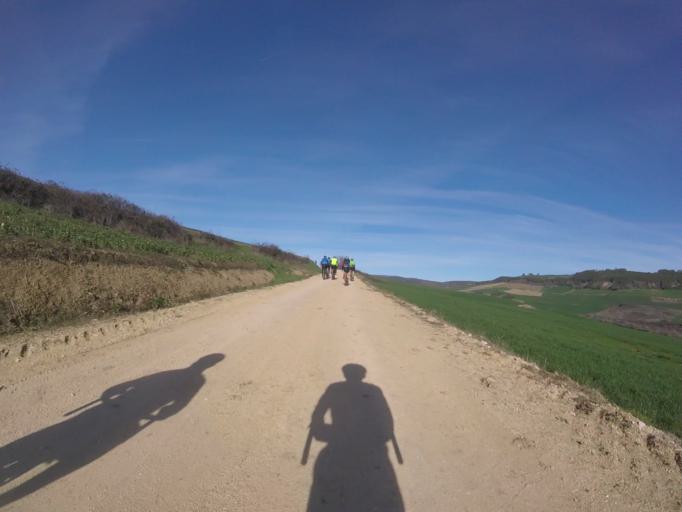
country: ES
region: Navarre
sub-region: Provincia de Navarra
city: Yerri
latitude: 42.7188
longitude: -1.9615
